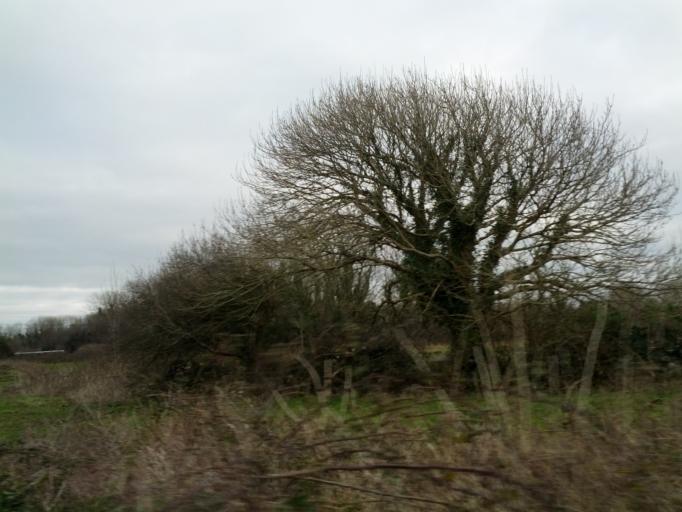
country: IE
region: Connaught
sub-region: County Galway
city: Oranmore
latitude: 53.1956
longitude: -8.9291
